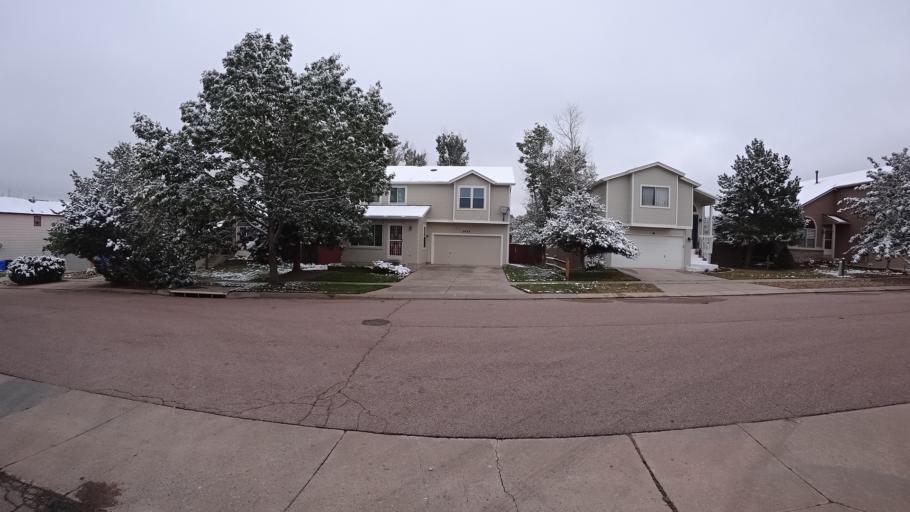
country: US
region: Colorado
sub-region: El Paso County
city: Colorado Springs
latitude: 38.9174
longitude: -104.7833
